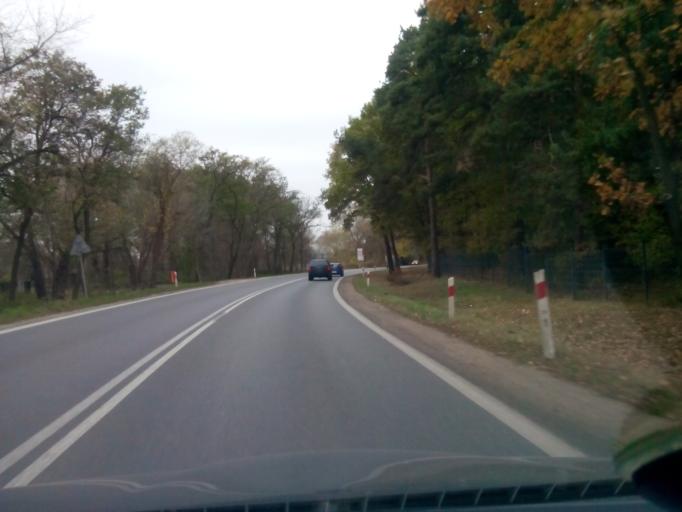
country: PL
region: Masovian Voivodeship
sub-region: Powiat pruszkowski
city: Granica
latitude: 52.1461
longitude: 20.7874
